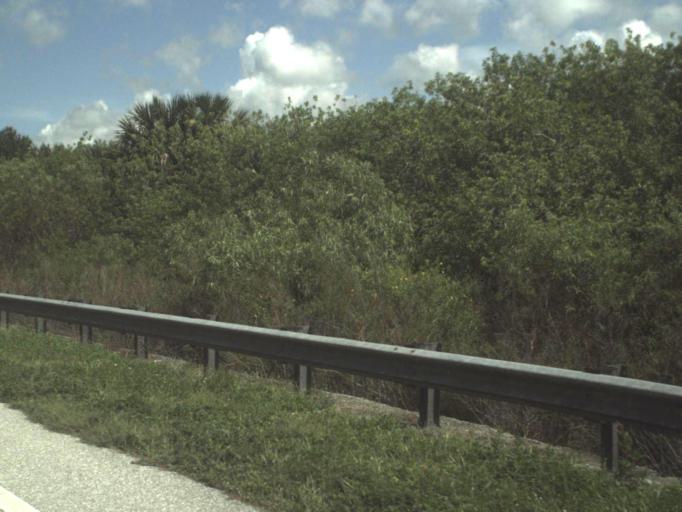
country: US
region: Florida
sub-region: Martin County
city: Indiantown
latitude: 27.0909
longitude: -80.5745
